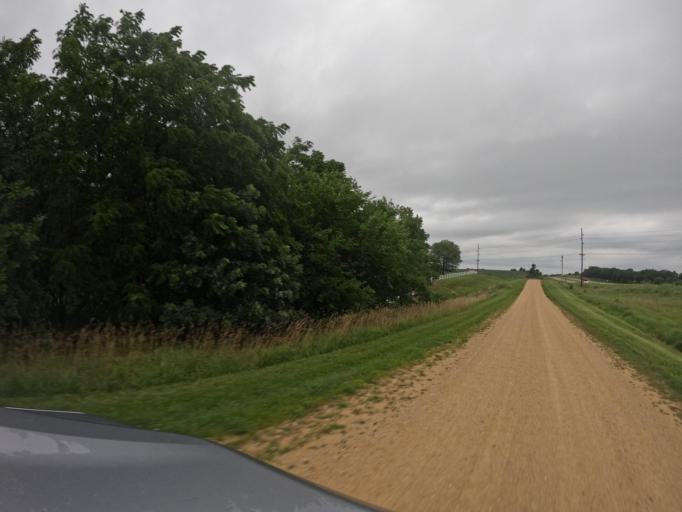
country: US
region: Iowa
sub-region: Clinton County
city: De Witt
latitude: 41.9371
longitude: -90.6172
